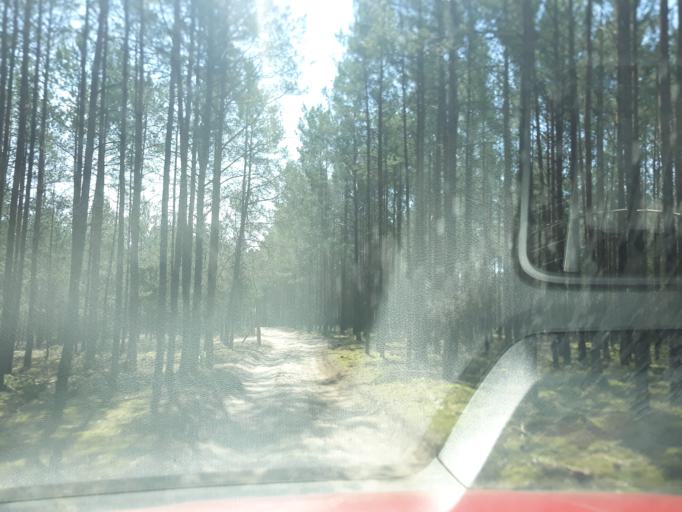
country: PL
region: Pomeranian Voivodeship
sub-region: Powiat chojnicki
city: Chojnice
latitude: 53.8700
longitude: 17.5416
